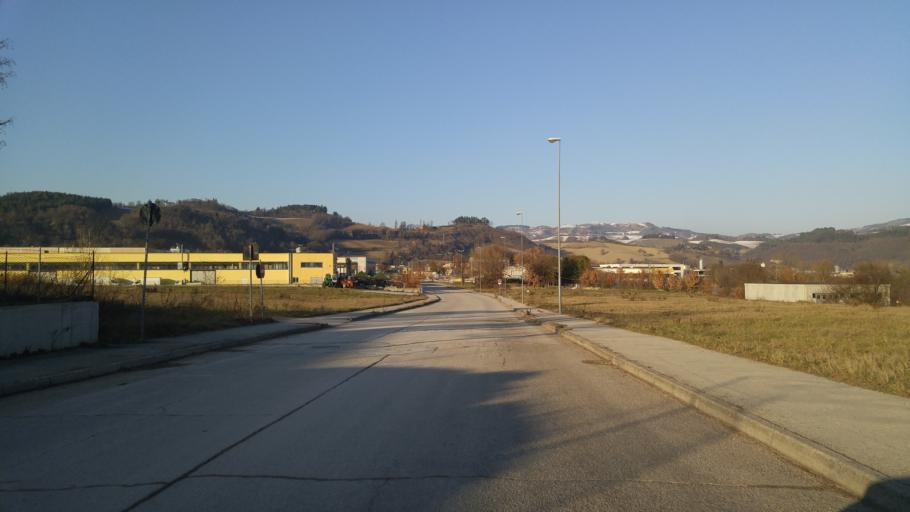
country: IT
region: The Marches
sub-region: Provincia di Pesaro e Urbino
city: Fermignano
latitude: 43.6862
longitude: 12.6480
